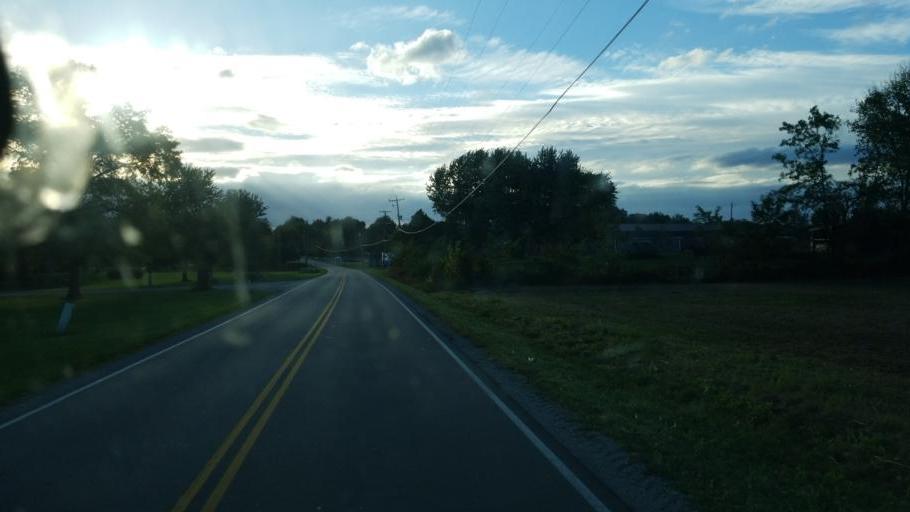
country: US
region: Ohio
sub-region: Franklin County
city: New Albany
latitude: 40.0535
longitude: -82.7341
